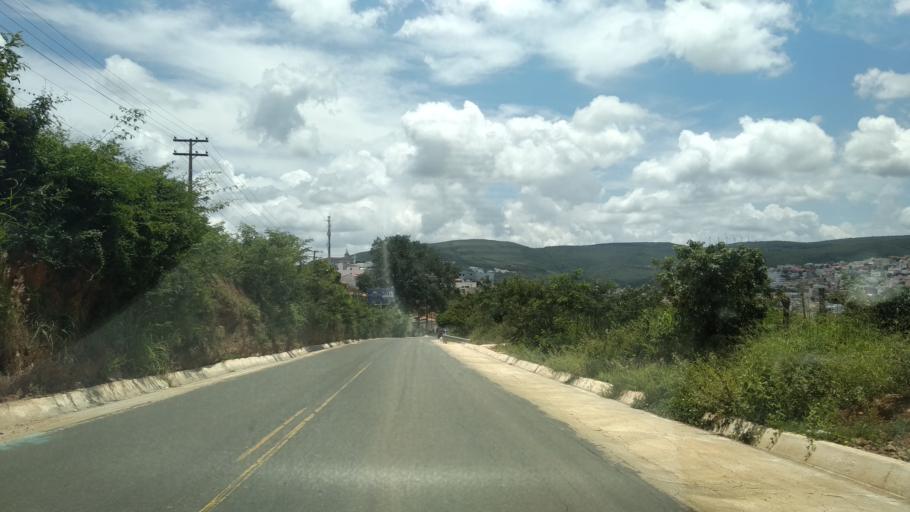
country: BR
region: Bahia
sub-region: Caetite
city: Caetite
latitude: -14.0602
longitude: -42.4910
